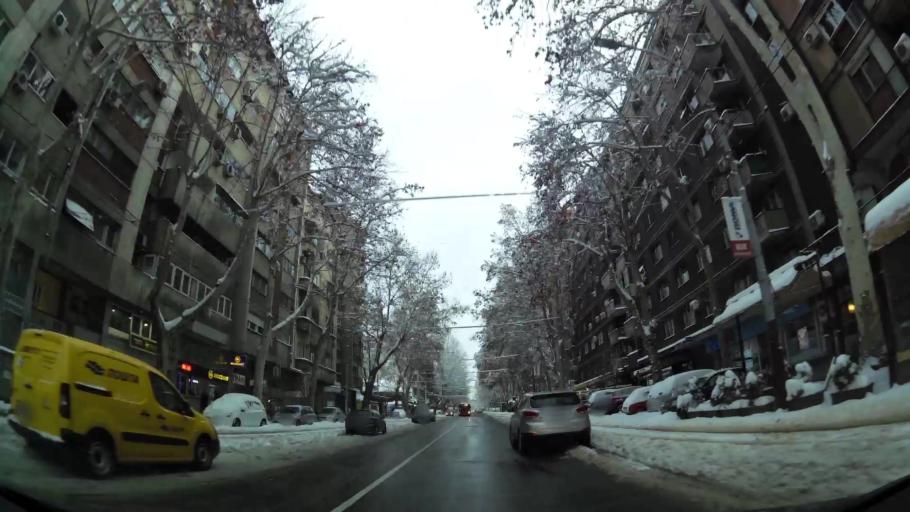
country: RS
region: Central Serbia
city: Belgrade
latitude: 44.8088
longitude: 20.4760
